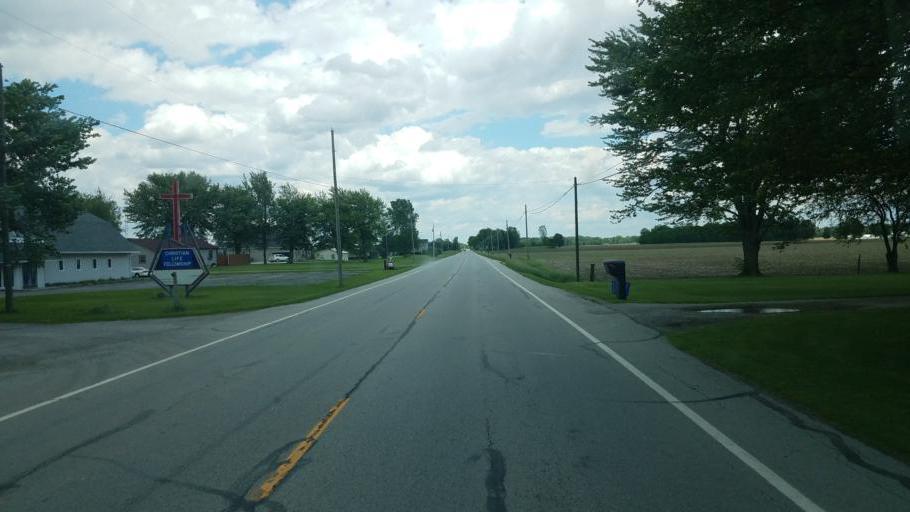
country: US
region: Ohio
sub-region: Crawford County
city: Bucyrus
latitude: 40.8129
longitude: -82.8834
